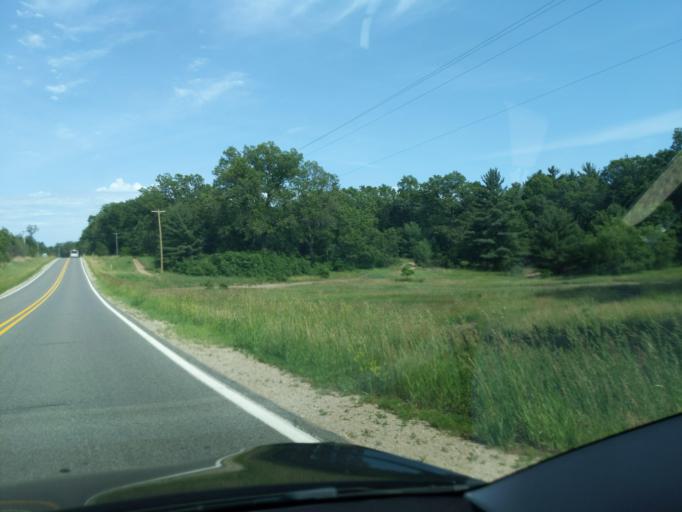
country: US
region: Michigan
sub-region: Muskegon County
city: Lakewood Club
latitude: 43.4096
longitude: -86.2958
